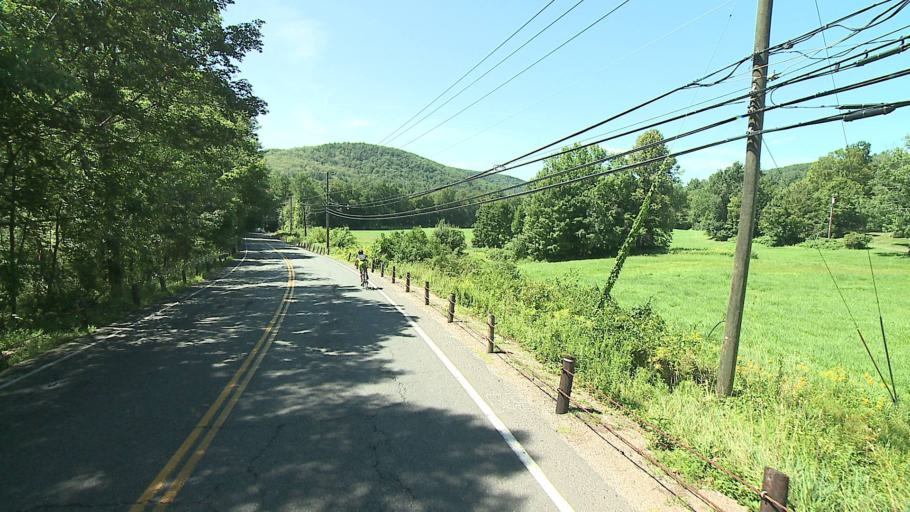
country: US
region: Connecticut
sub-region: Litchfield County
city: New Hartford Center
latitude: 41.9135
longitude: -72.9820
